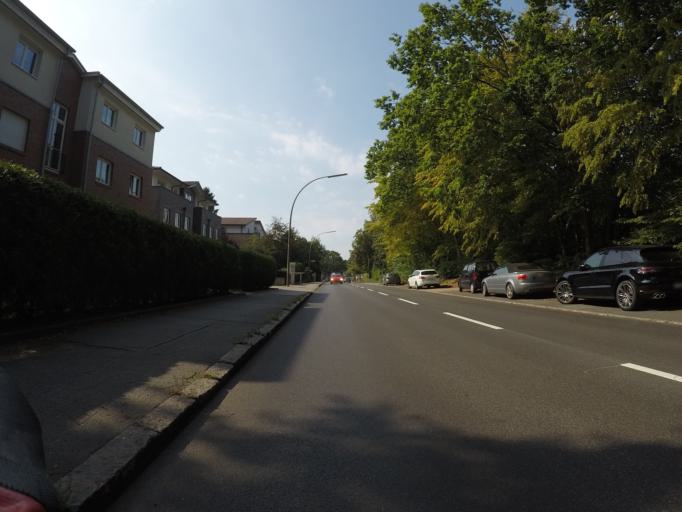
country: DE
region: Hamburg
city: Wellingsbuettel
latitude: 53.6431
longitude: 10.0833
